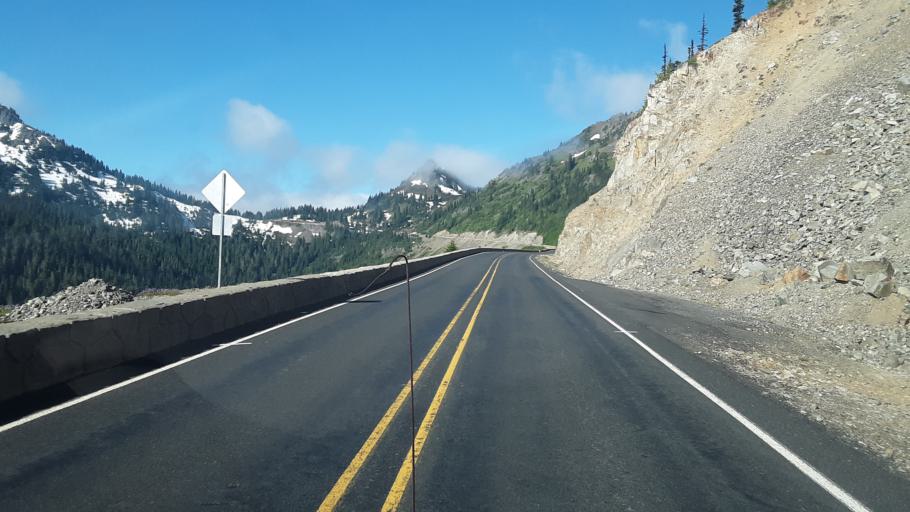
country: US
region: Washington
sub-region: King County
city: Enumclaw
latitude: 46.8879
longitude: -121.5005
